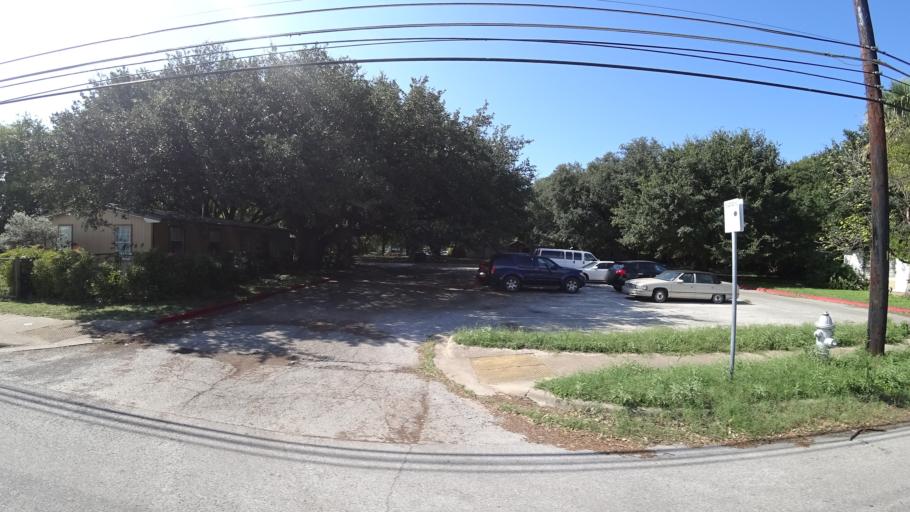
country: US
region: Texas
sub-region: Travis County
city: Austin
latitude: 30.2531
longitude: -97.7312
